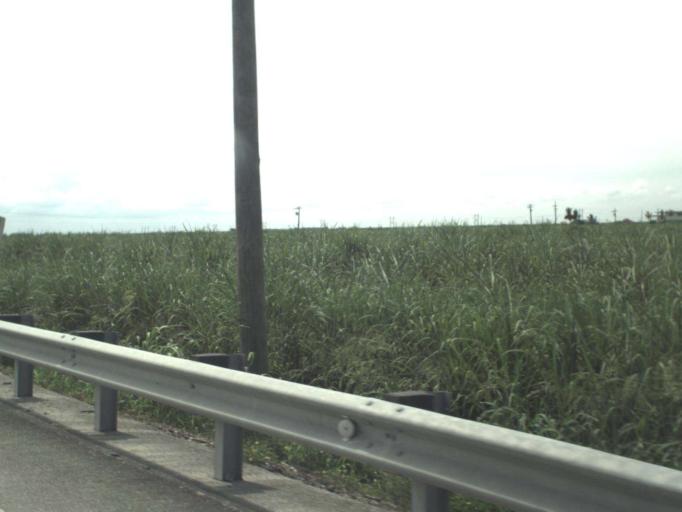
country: US
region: Florida
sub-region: Palm Beach County
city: Pahokee
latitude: 26.7863
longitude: -80.6534
